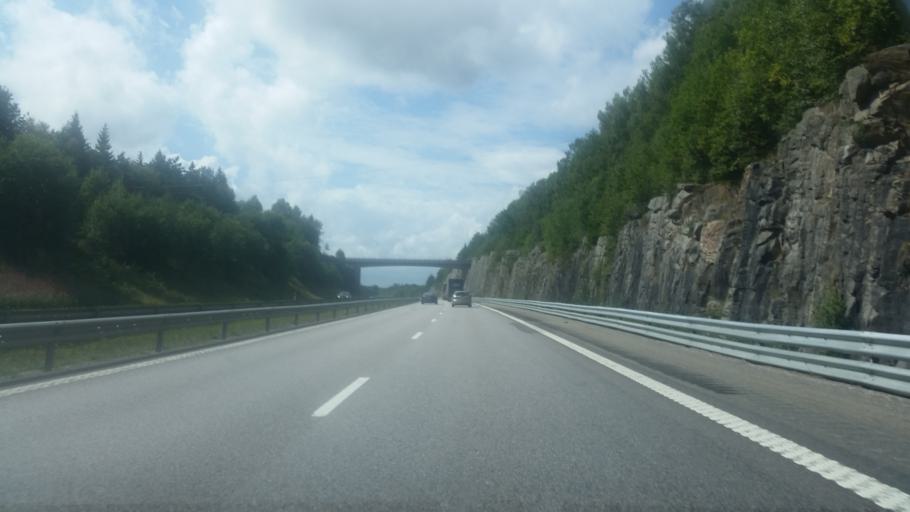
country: SE
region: Vaestra Goetaland
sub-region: Boras Kommun
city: Sandared
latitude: 57.6809
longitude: 12.7192
